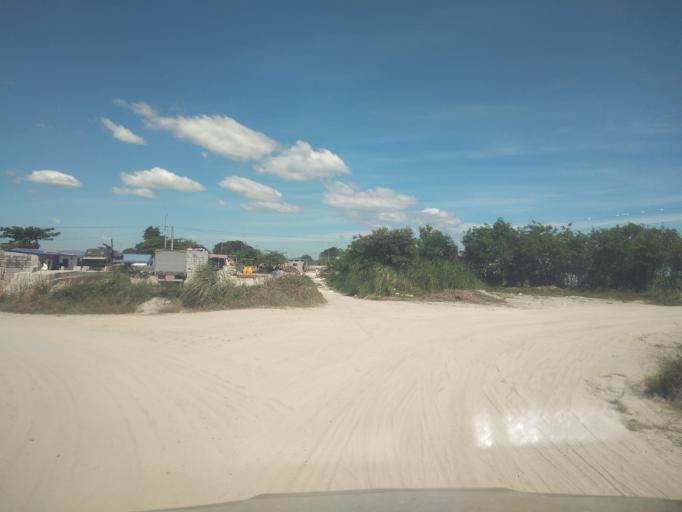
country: PH
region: Central Luzon
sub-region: Province of Pampanga
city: San Basilio
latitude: 15.0216
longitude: 120.6032
